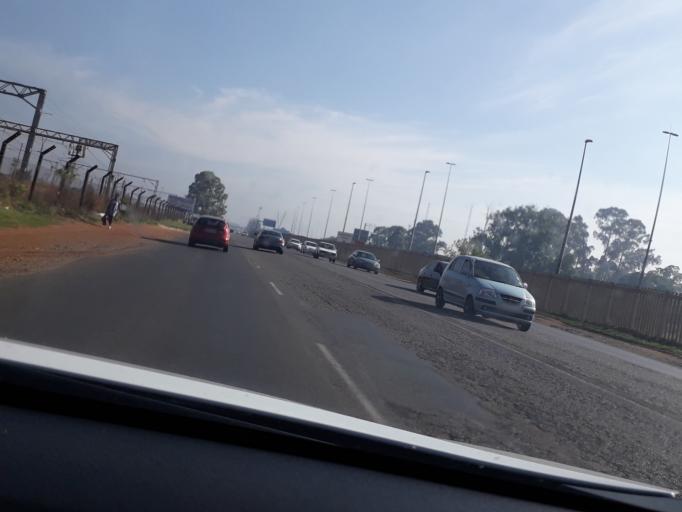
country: ZA
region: Gauteng
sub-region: City of Johannesburg Metropolitan Municipality
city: Modderfontein
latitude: -26.1439
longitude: 28.2191
